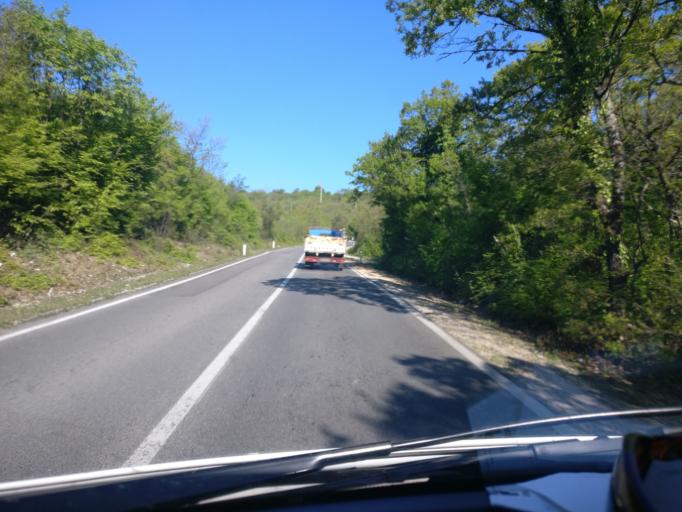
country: BA
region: Federation of Bosnia and Herzegovina
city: Crnici
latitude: 43.1015
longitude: 17.9068
